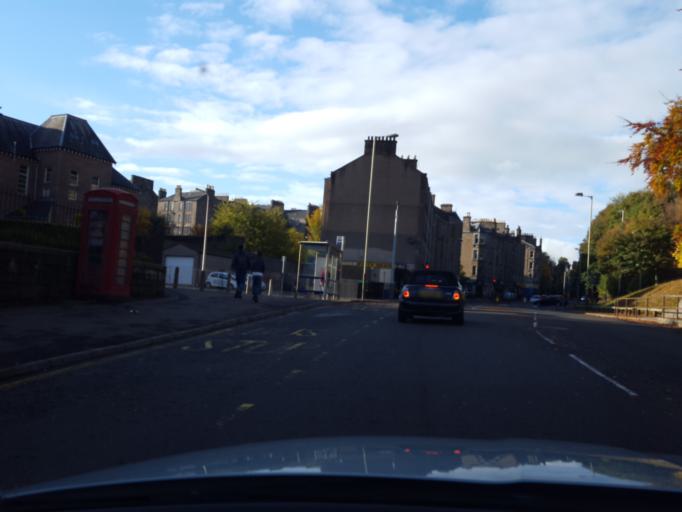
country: GB
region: Scotland
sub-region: Dundee City
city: Dundee
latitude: 56.4638
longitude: -2.9915
